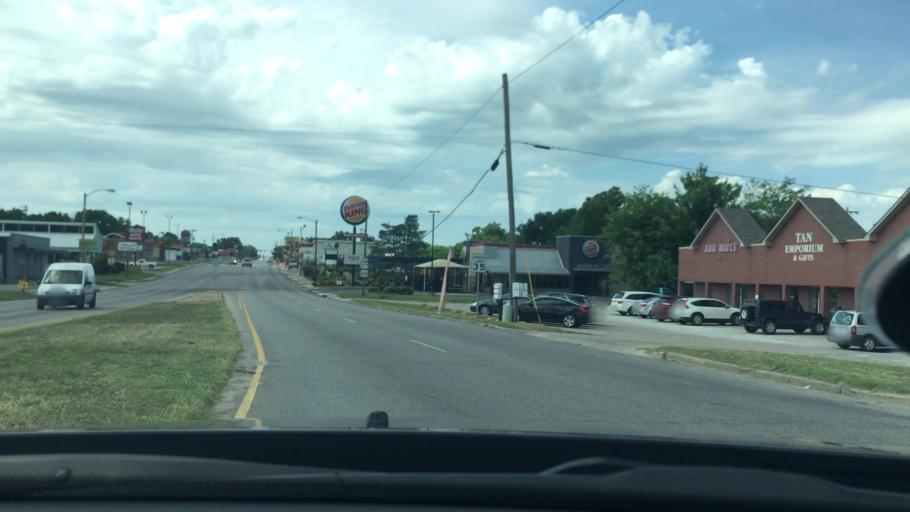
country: US
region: Oklahoma
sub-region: Pontotoc County
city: Ada
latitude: 34.7813
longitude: -96.6700
